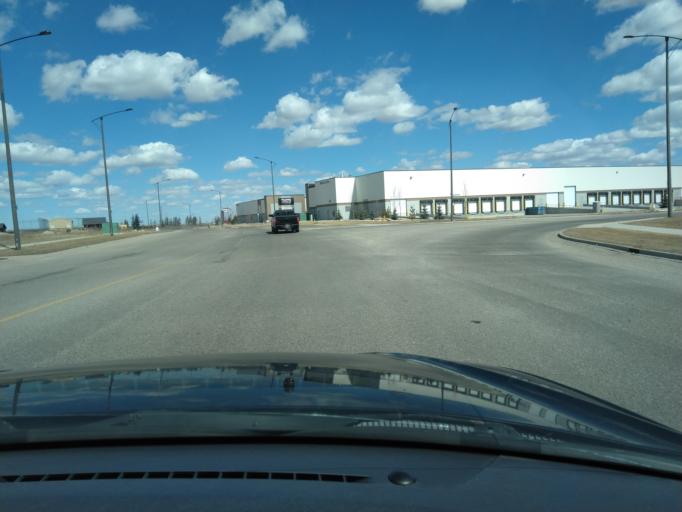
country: CA
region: Alberta
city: Calgary
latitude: 51.1329
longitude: -114.0368
